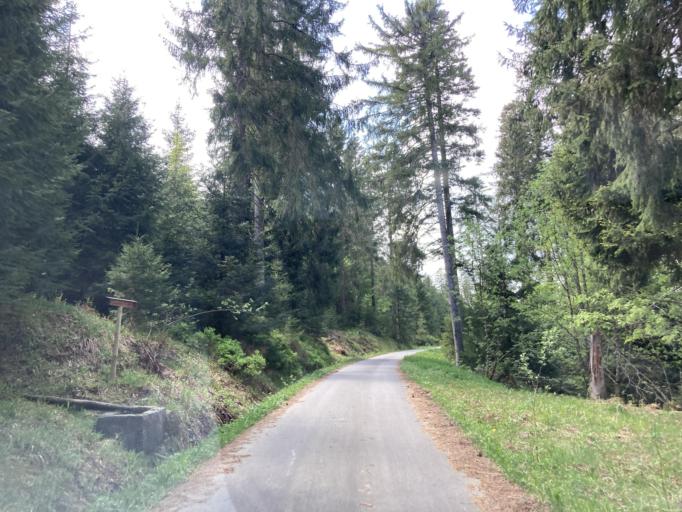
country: DE
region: Baden-Wuerttemberg
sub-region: Freiburg Region
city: Bad Peterstal-Griesbach
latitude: 48.4983
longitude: 8.2600
